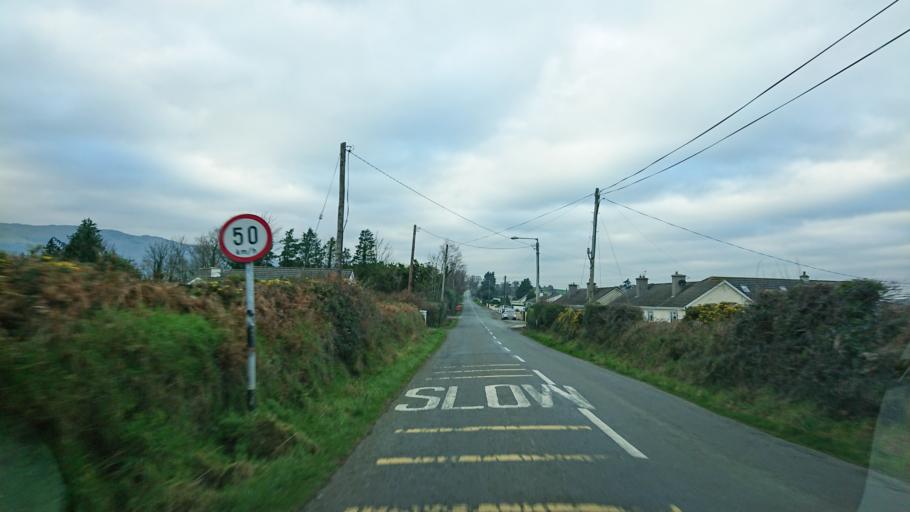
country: IE
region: Munster
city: Carrick-on-Suir
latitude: 52.3099
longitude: -7.5133
